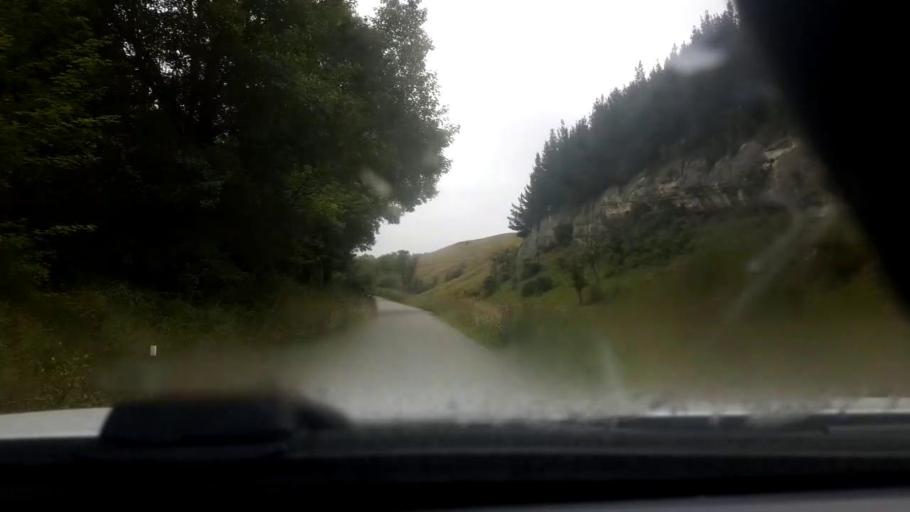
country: NZ
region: Canterbury
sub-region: Timaru District
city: Pleasant Point
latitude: -44.1953
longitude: 171.0718
